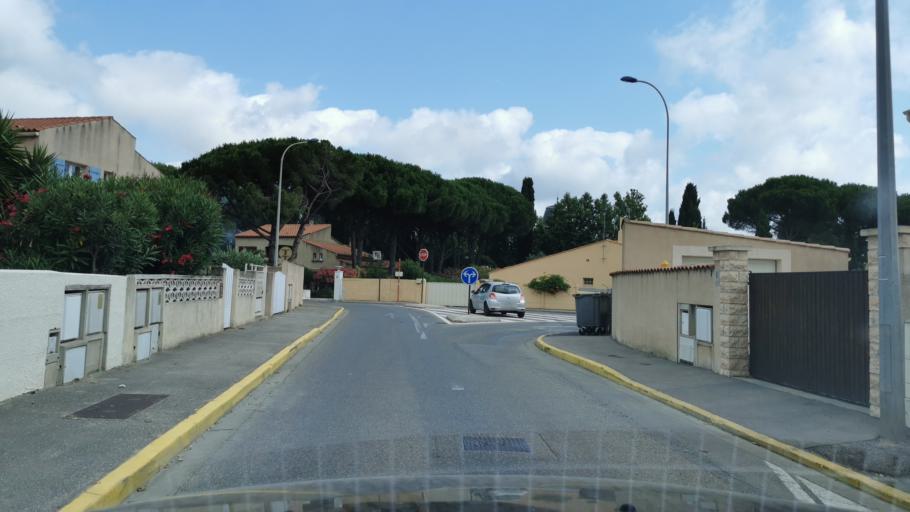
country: FR
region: Languedoc-Roussillon
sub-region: Departement de l'Aude
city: Narbonne
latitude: 43.1969
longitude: 3.0149
